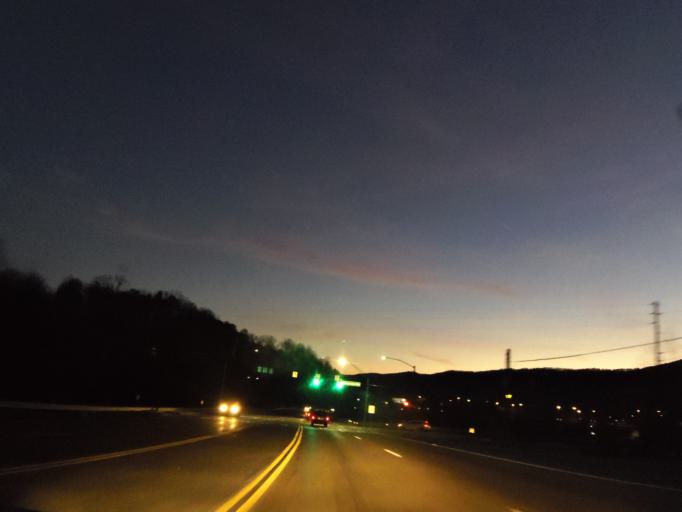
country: US
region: Georgia
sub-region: Whitfield County
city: Dalton
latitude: 34.7994
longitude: -84.9935
